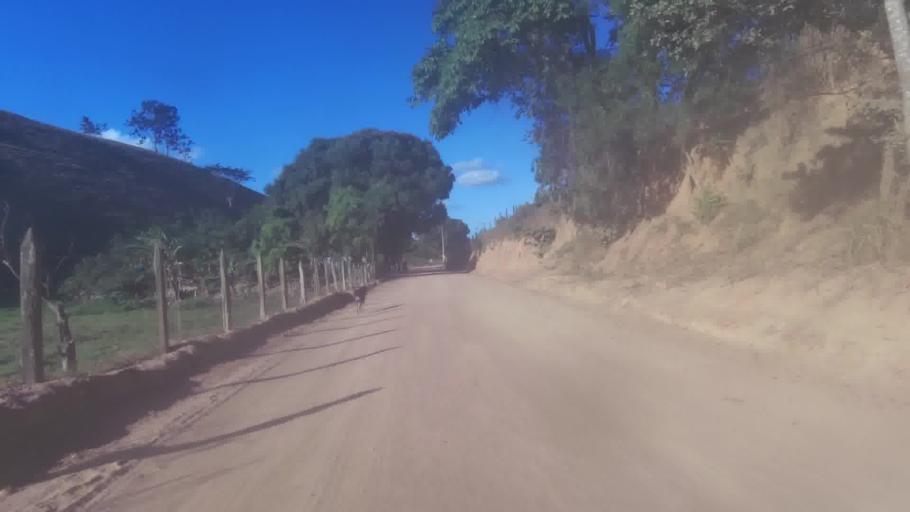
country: BR
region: Espirito Santo
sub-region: Mimoso Do Sul
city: Mimoso do Sul
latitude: -21.1025
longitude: -41.1274
